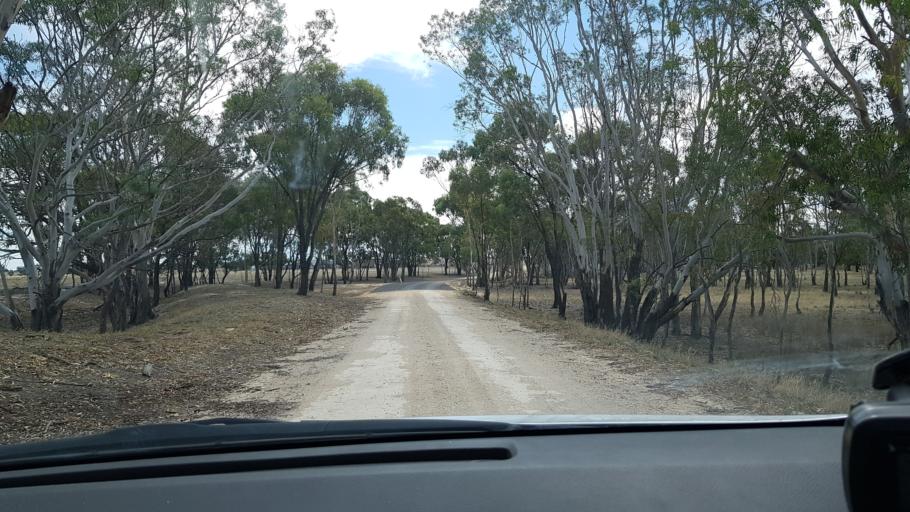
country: AU
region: Victoria
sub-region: Horsham
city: Horsham
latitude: -36.6847
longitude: 141.7758
